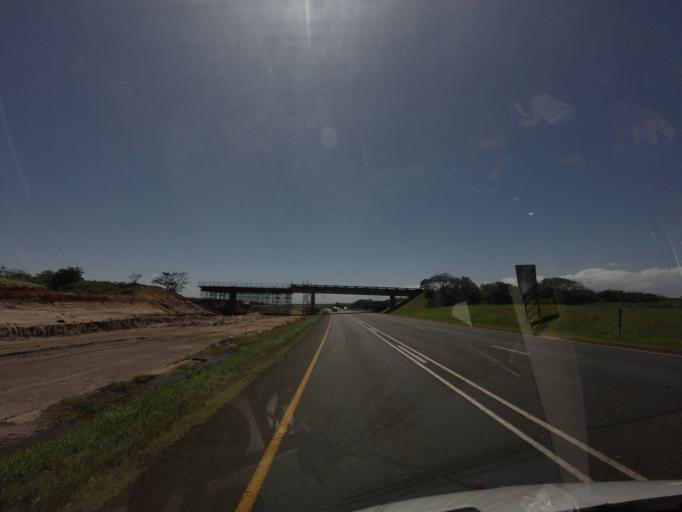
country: ZA
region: KwaZulu-Natal
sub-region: uThungulu District Municipality
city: eSikhawini
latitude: -28.9302
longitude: 31.7845
